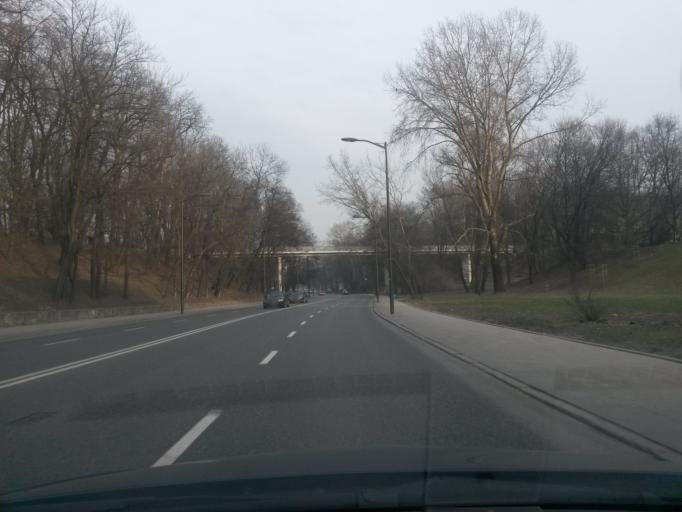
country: PL
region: Masovian Voivodeship
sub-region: Warszawa
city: Srodmiescie
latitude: 52.2299
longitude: 21.0257
